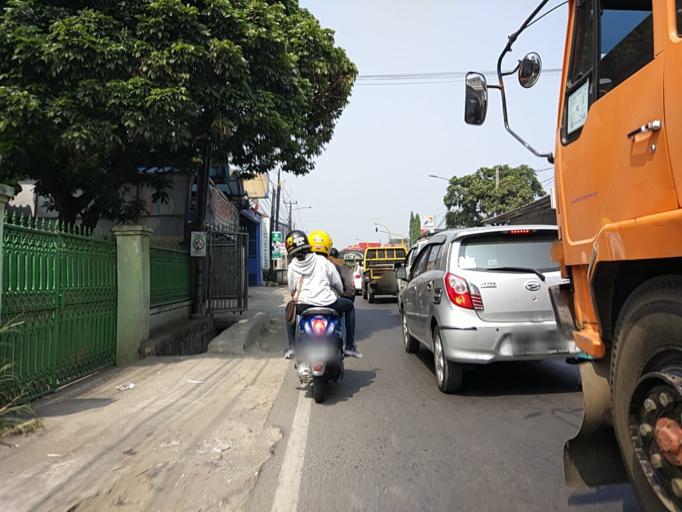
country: ID
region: West Java
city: Padalarang
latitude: -6.8548
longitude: 107.4982
